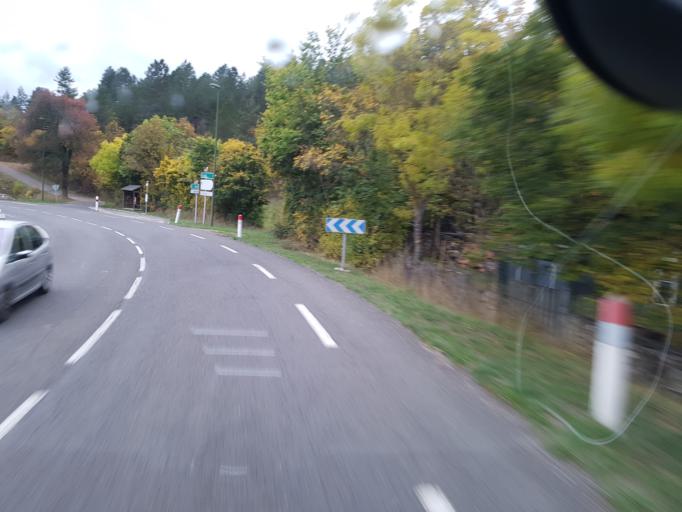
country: FR
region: Languedoc-Roussillon
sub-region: Departement de la Lozere
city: Mende
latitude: 44.5396
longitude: 3.6081
